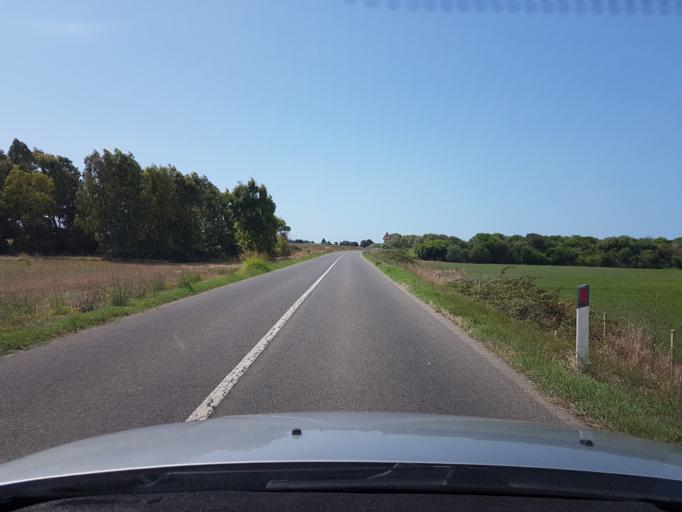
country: IT
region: Sardinia
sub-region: Provincia di Oristano
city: Riola Sardo
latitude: 40.0205
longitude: 8.4845
